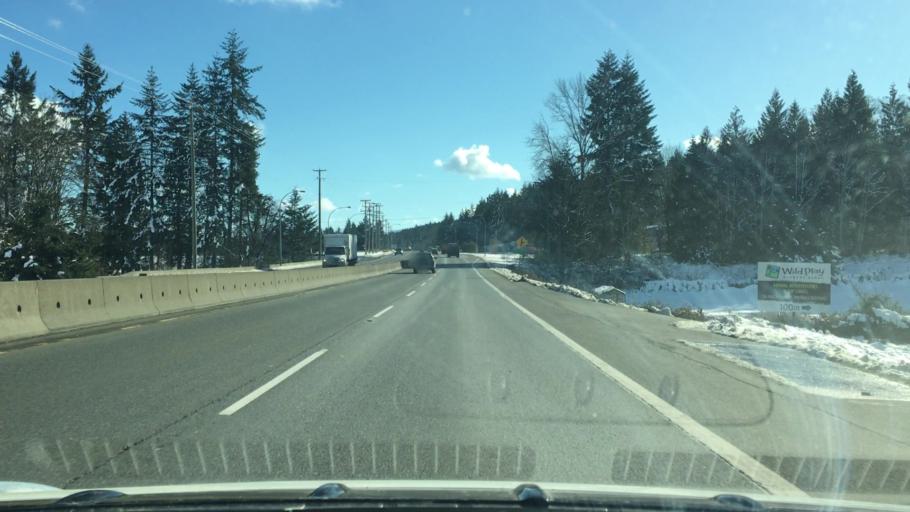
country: CA
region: British Columbia
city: Nanaimo
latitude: 49.0780
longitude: -123.8822
